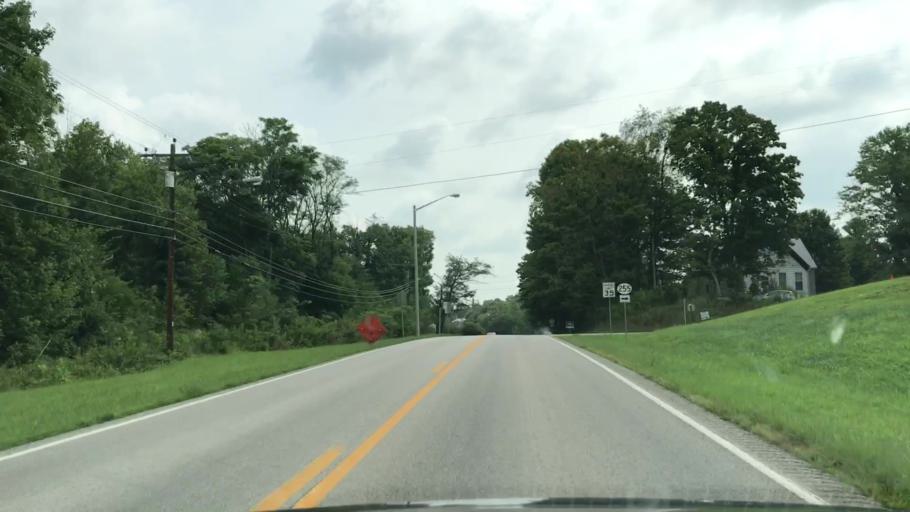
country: US
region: Kentucky
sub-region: Barren County
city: Cave City
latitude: 37.0923
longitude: -86.0558
